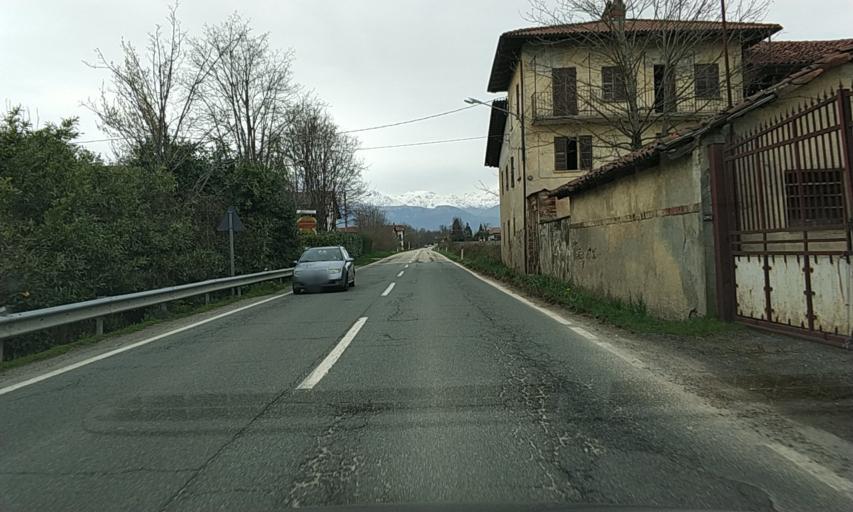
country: IT
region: Piedmont
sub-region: Provincia di Torino
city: Favria
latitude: 45.3081
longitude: 7.6779
